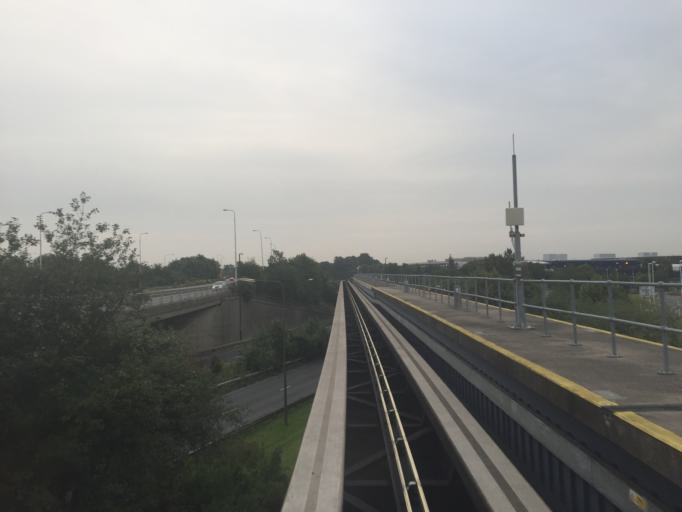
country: GB
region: England
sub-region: Surrey
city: Horley
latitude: 51.1601
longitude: -0.1657
